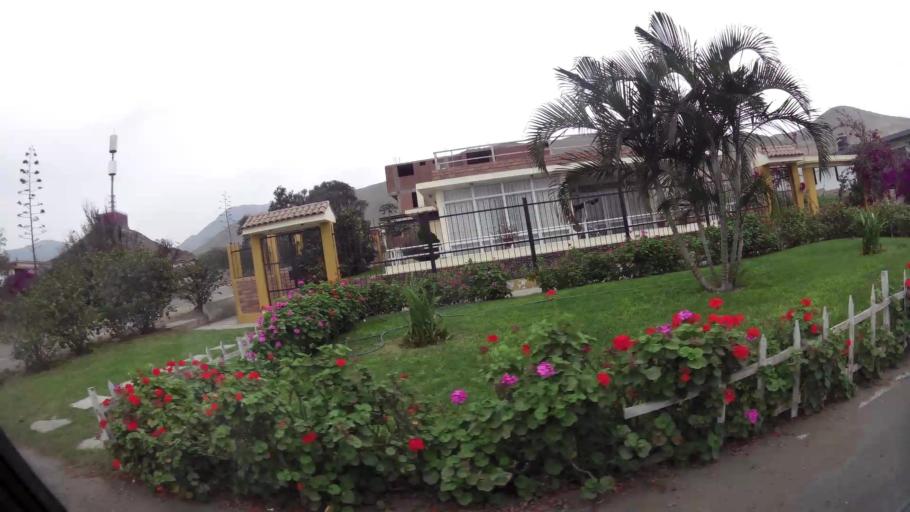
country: PE
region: Lima
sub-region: Lima
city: Santa Rosa
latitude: -11.8033
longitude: -77.1734
